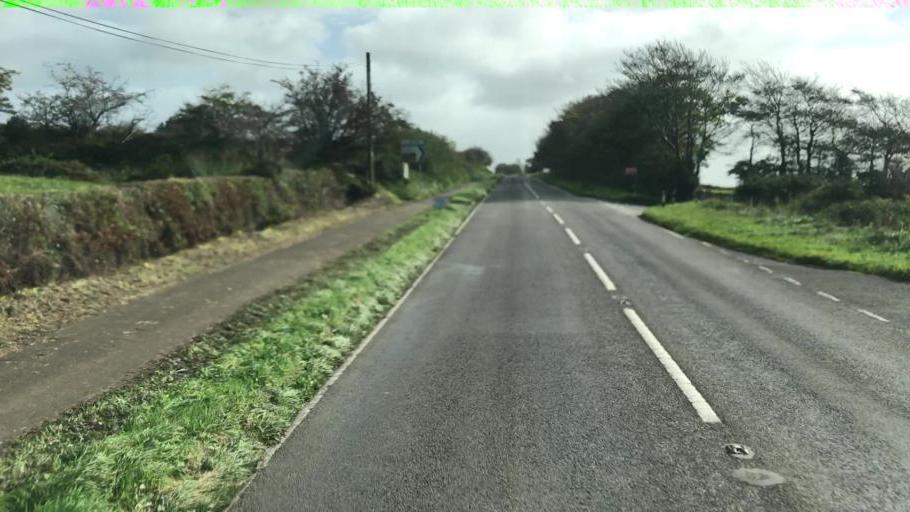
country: GB
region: England
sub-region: Cornwall
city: Callington
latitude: 50.5166
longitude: -4.2656
